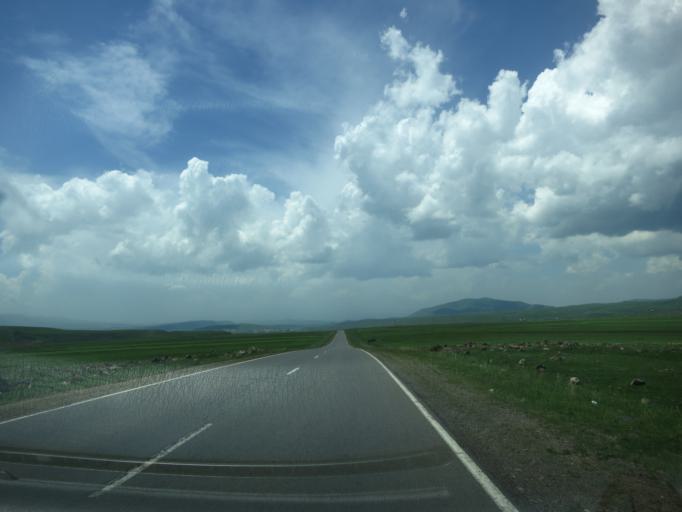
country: GE
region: Samtskhe-Javakheti
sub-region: Ninotsminda
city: Ninotsminda
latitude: 41.2931
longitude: 43.6928
